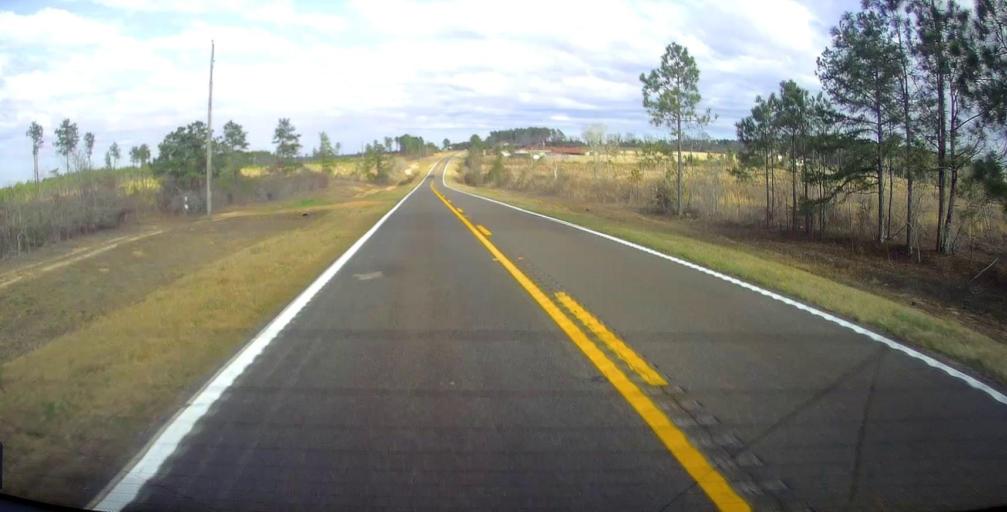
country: US
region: Georgia
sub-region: Marion County
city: Buena Vista
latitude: 32.4448
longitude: -84.5301
